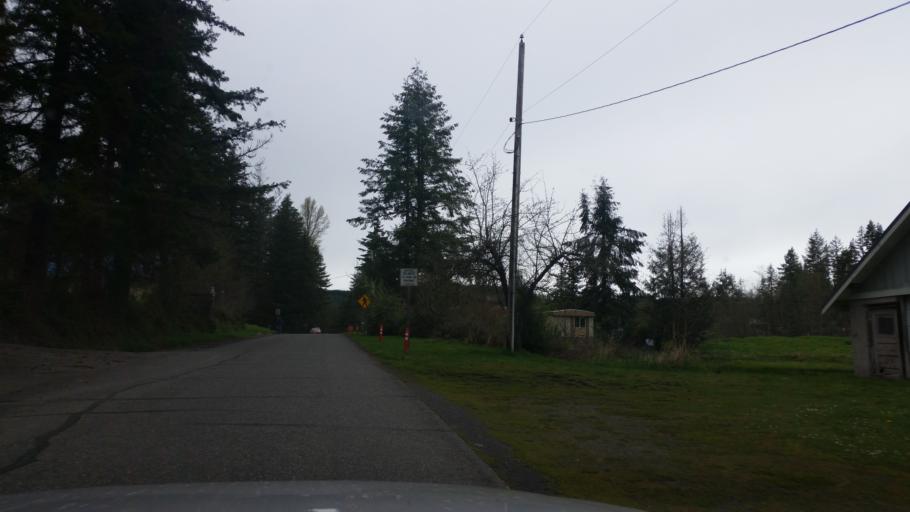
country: US
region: Washington
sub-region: Pierce County
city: Eatonville
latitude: 46.8002
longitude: -122.2916
